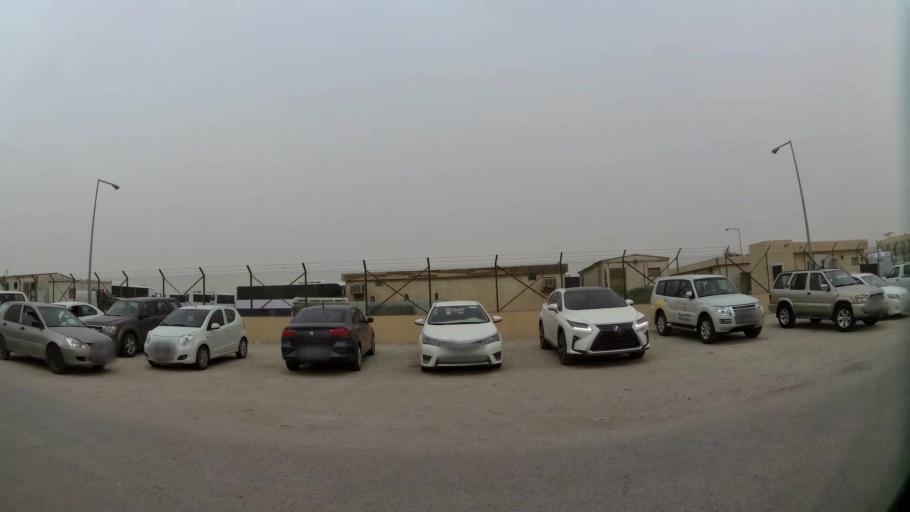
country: QA
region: Baladiyat ad Dawhah
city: Doha
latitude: 25.2382
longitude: 51.5065
